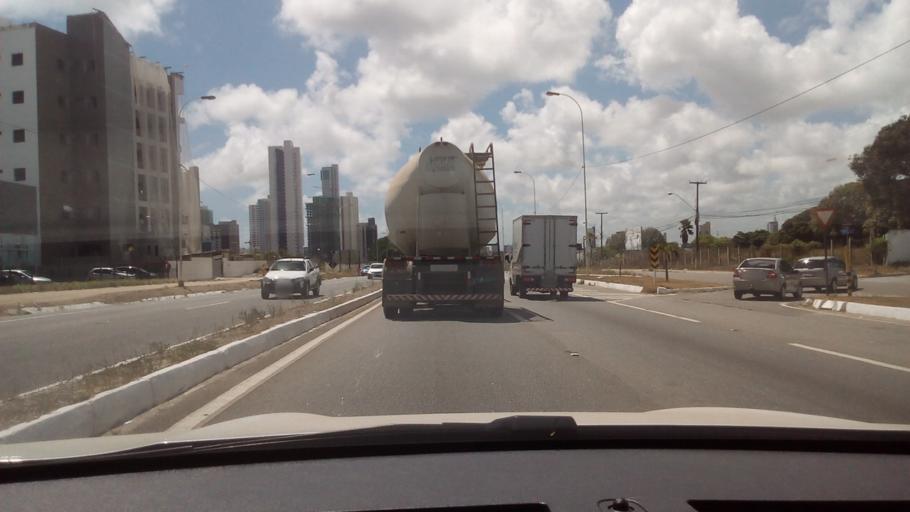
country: BR
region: Paraiba
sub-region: Joao Pessoa
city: Joao Pessoa
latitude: -7.1070
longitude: -34.8438
